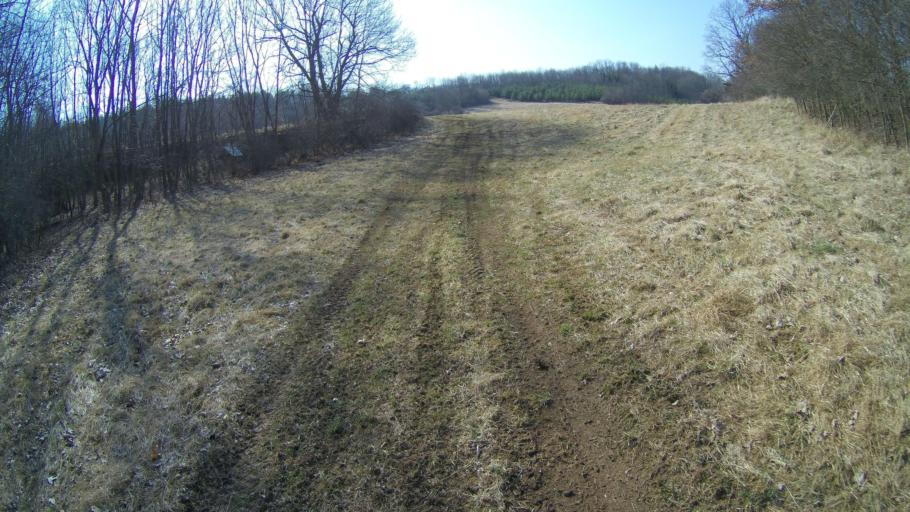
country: CZ
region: Ustecky
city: Mecholupy
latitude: 50.2684
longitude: 13.5539
